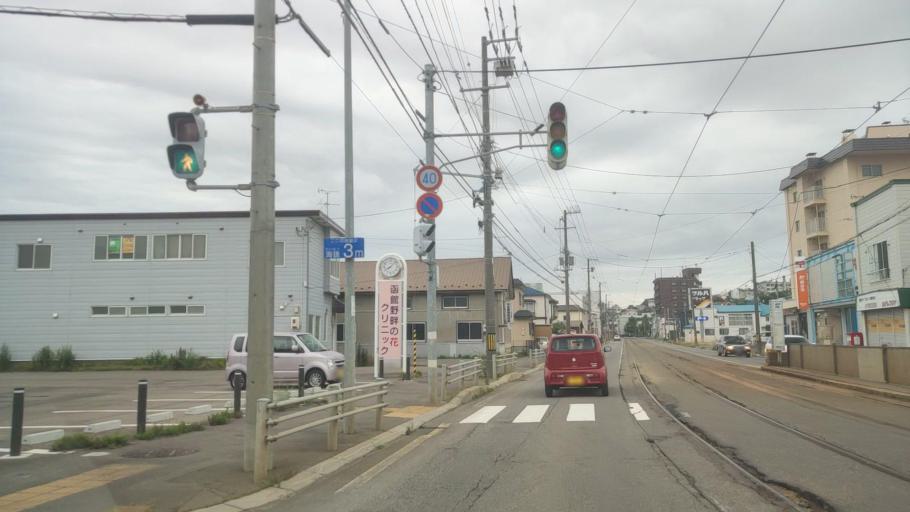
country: JP
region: Hokkaido
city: Hakodate
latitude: 41.7700
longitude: 140.7094
